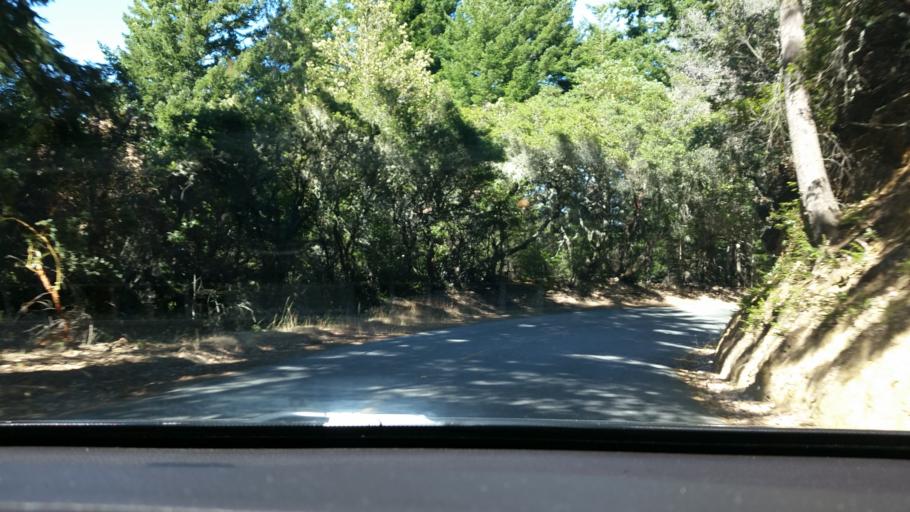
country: US
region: California
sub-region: San Mateo County
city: Woodside
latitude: 37.4291
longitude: -122.3018
